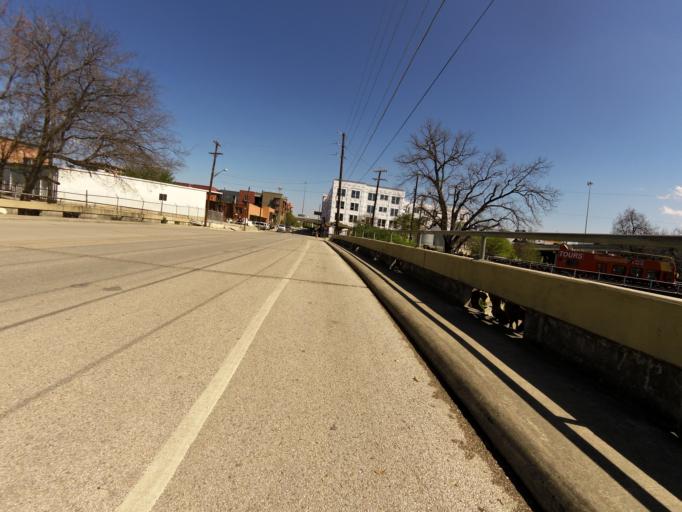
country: US
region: Texas
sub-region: Bexar County
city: San Antonio
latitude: 29.4408
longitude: -98.4825
